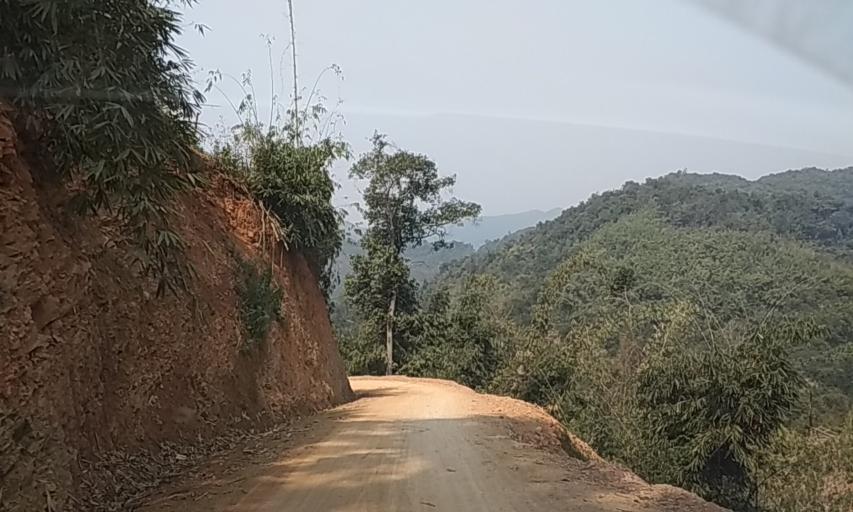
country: LA
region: Phongsali
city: Phongsali
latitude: 21.4724
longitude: 102.4335
